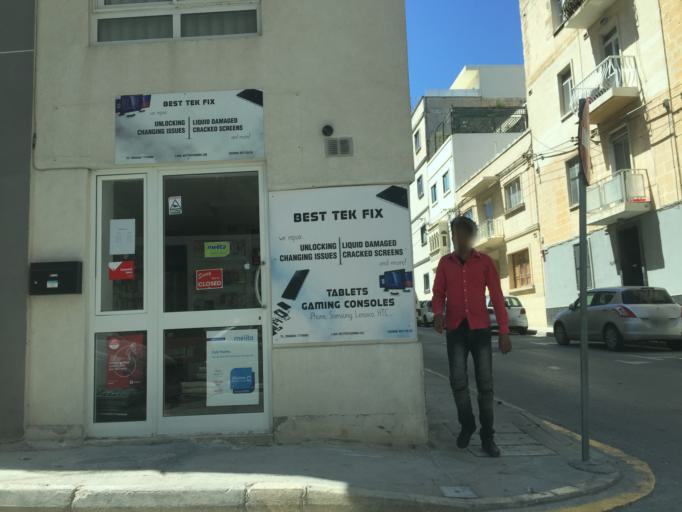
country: MT
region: Il-Gzira
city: Gzira
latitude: 35.8992
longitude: 14.4873
